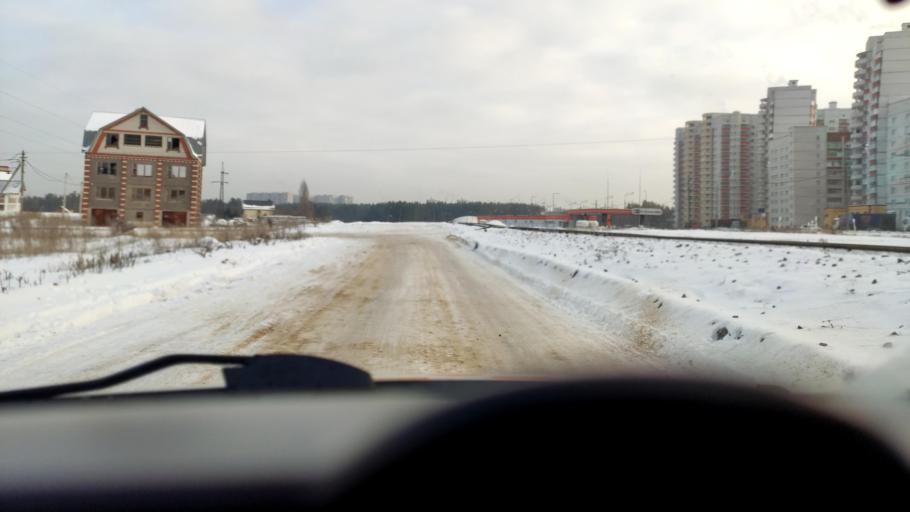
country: RU
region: Voronezj
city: Podgornoye
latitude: 51.7260
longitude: 39.1607
